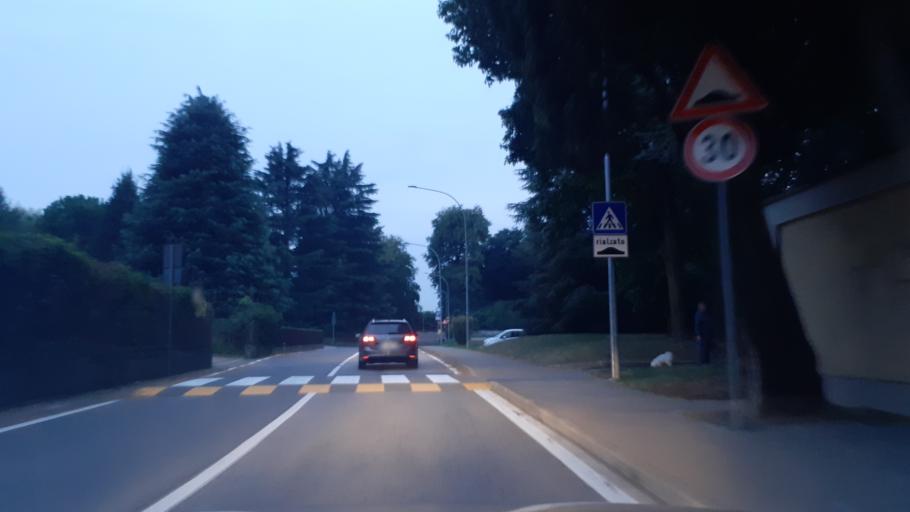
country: IT
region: Lombardy
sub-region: Provincia di Lecco
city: Bulciago
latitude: 45.7563
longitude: 9.2888
